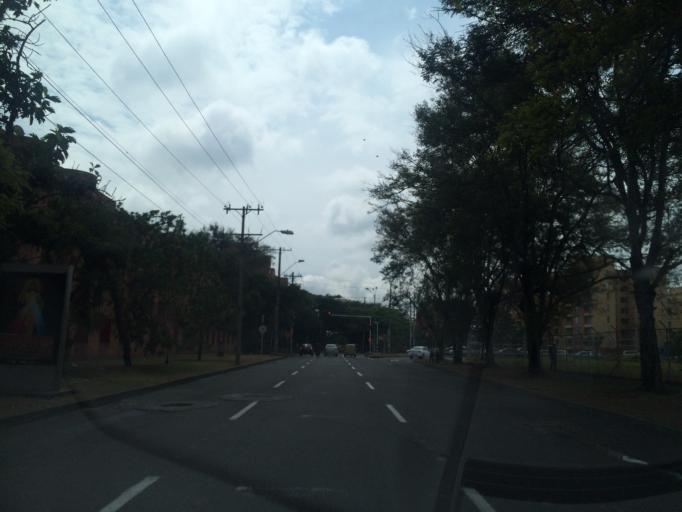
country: CO
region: Valle del Cauca
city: Cali
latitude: 3.3797
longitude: -76.5300
